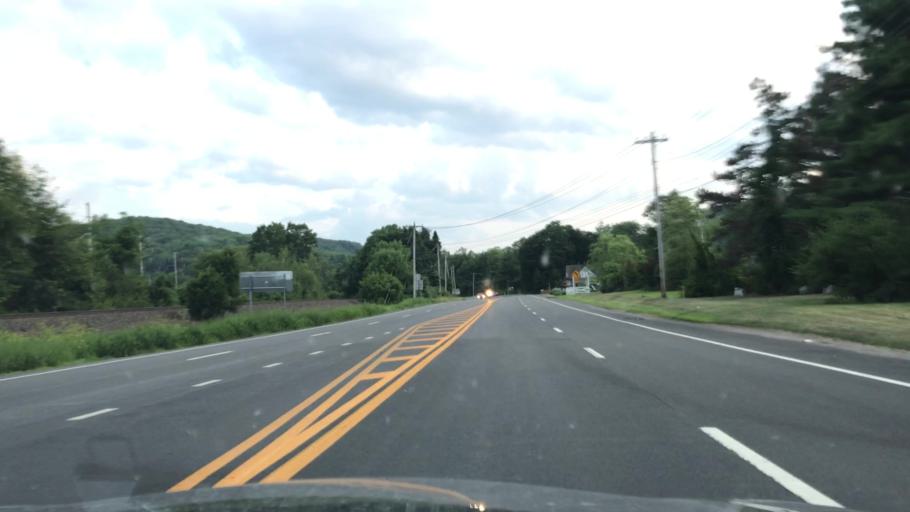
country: US
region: New York
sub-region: Rockland County
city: Sloatsburg
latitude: 41.2267
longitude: -74.1861
